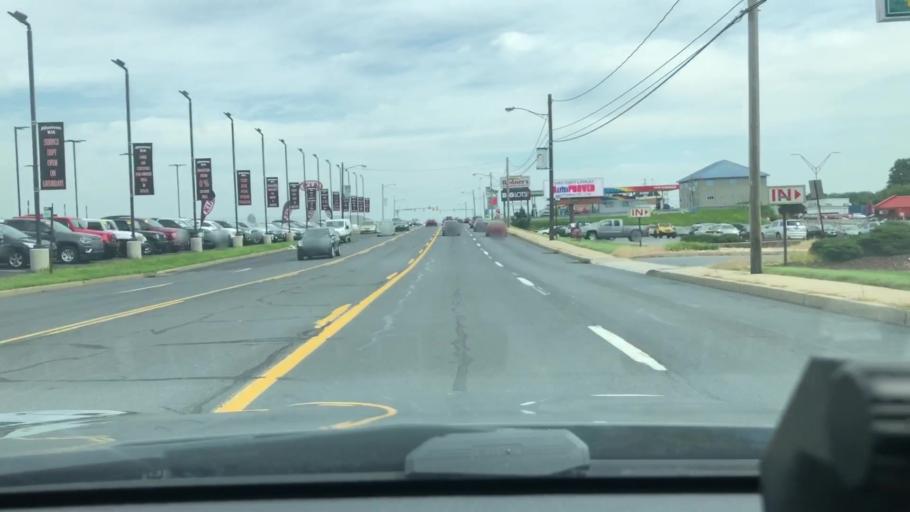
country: US
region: Pennsylvania
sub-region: Lehigh County
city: Emmaus
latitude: 40.5694
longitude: -75.4822
